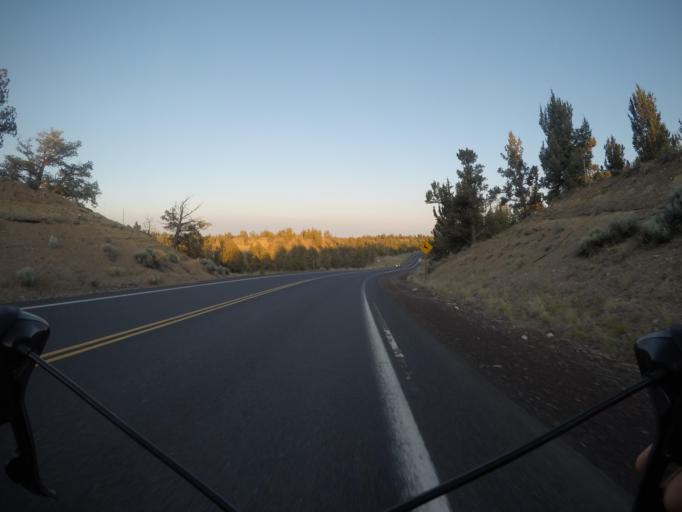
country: US
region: Oregon
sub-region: Deschutes County
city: Redmond
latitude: 44.2734
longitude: -121.2618
